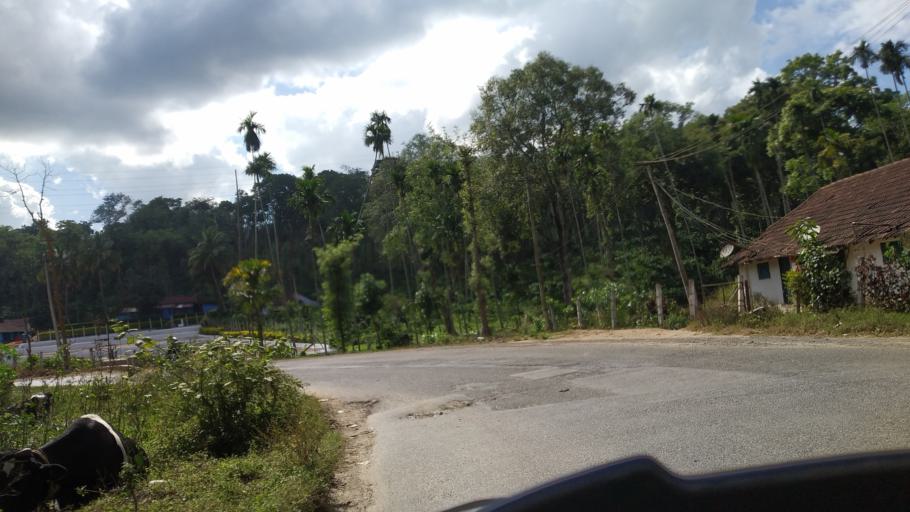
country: IN
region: Karnataka
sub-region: Kodagu
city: Ponnampet
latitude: 11.9642
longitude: 76.0560
